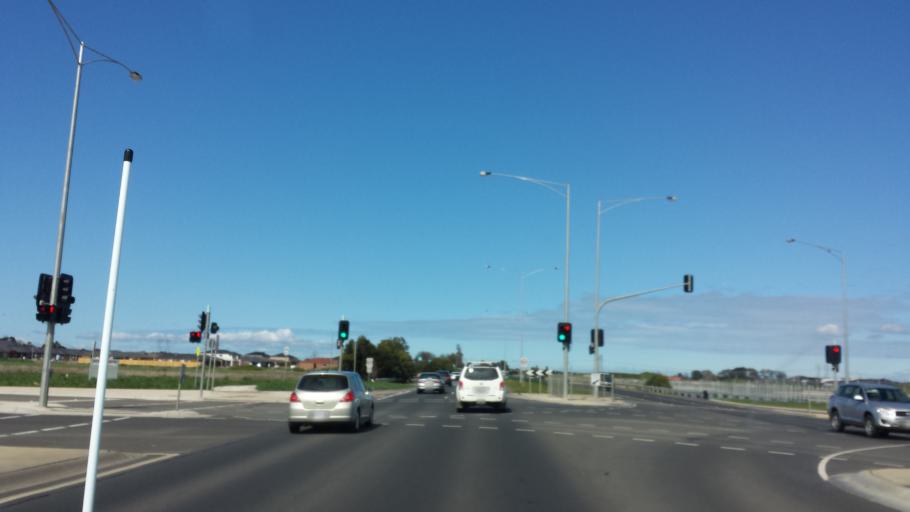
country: AU
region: Victoria
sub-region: Casey
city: Cranbourne East
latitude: -38.0822
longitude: 145.3341
